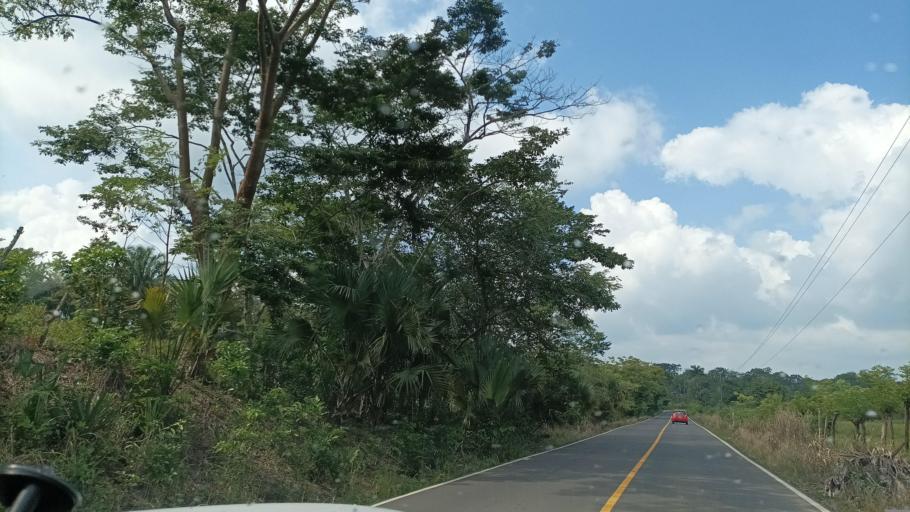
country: MX
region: Tabasco
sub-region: Huimanguillo
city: Francisco Rueda
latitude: 17.7334
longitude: -94.1045
